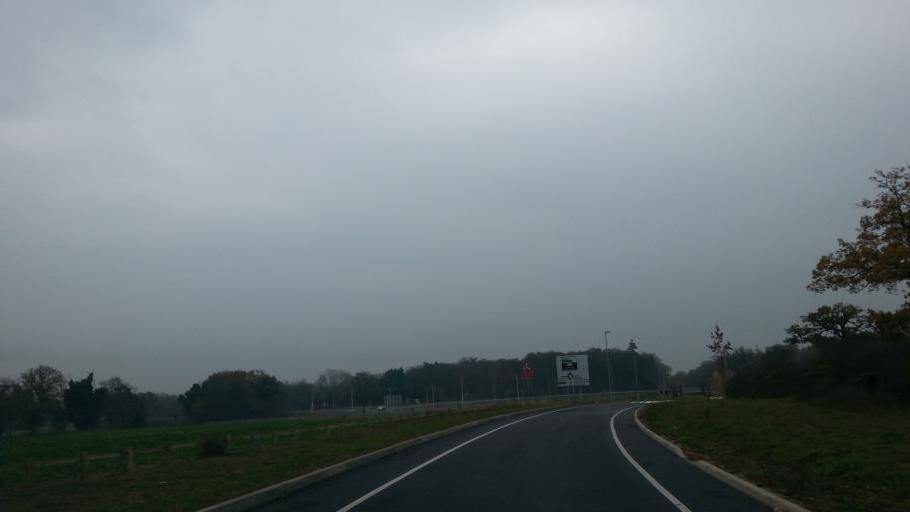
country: GB
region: England
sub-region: Suffolk
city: Thurston
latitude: 52.2416
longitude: 0.7819
